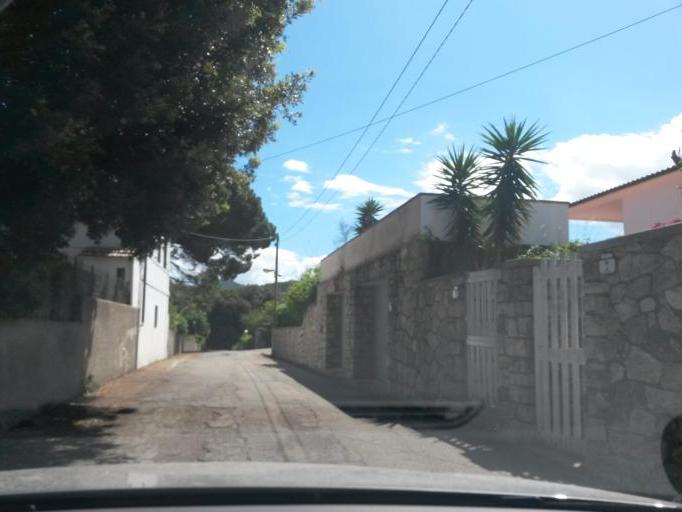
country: IT
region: Tuscany
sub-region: Provincia di Livorno
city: Rio Marina
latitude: 42.8651
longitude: 10.4197
